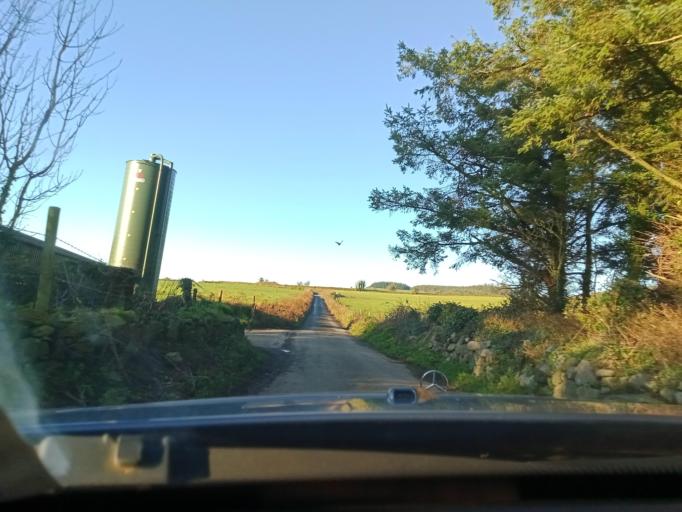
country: IE
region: Leinster
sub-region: Kilkenny
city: Callan
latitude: 52.4609
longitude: -7.4146
